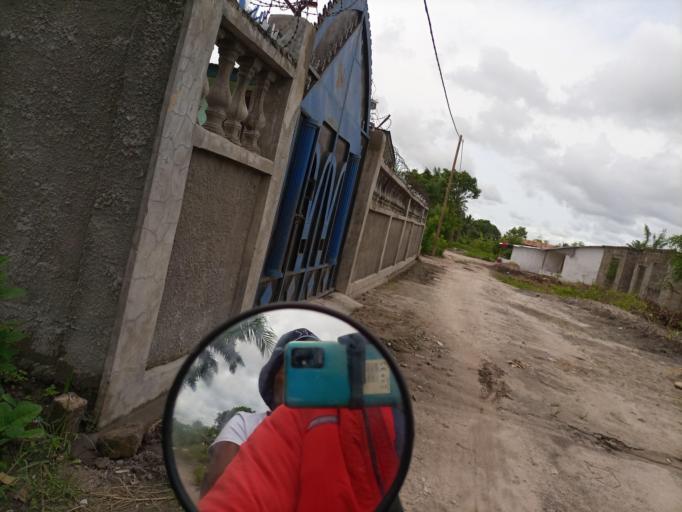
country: SL
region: Southern Province
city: Bo
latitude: 7.9419
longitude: -11.7444
